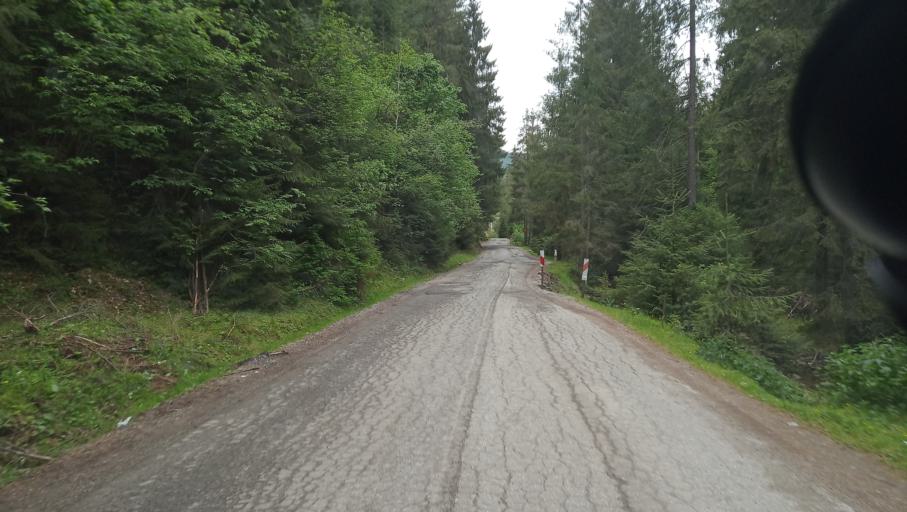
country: RO
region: Alba
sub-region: Comuna Horea
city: Horea
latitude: 46.5093
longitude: 22.9218
